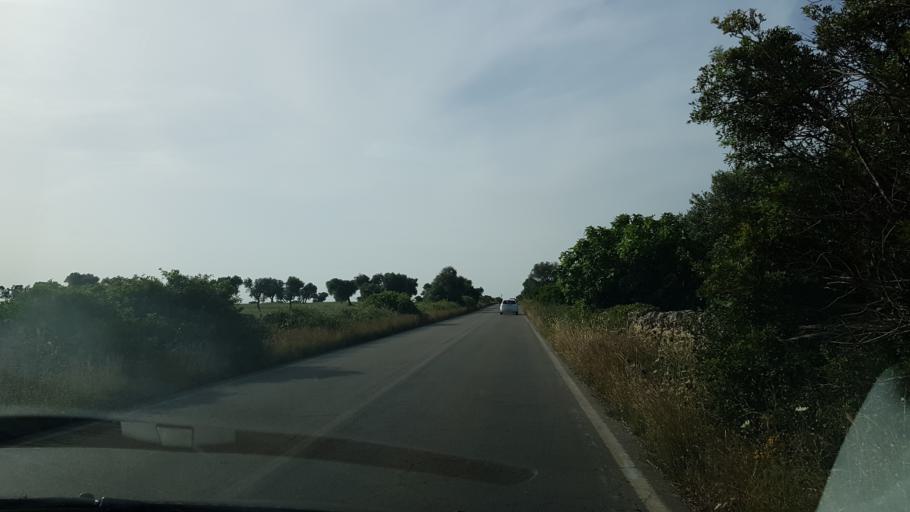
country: IT
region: Apulia
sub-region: Provincia di Lecce
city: Porto Cesareo
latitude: 40.3142
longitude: 17.8619
